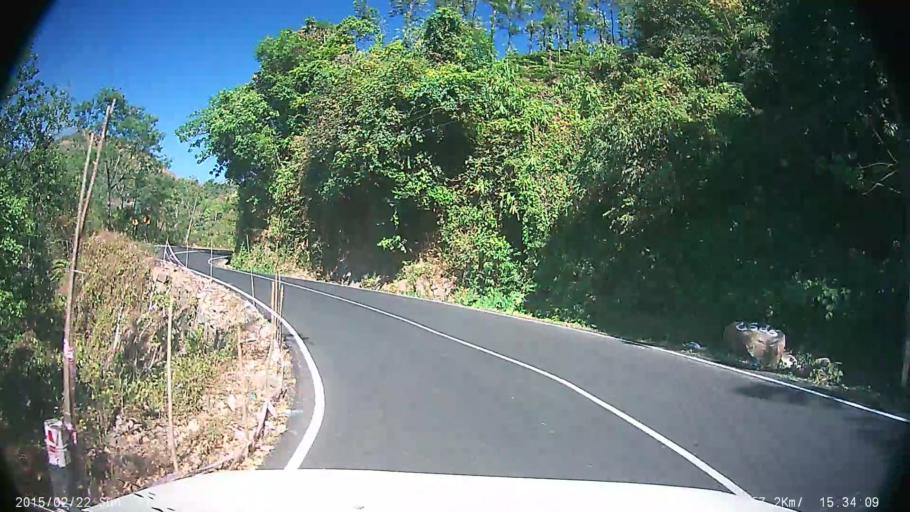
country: IN
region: Kerala
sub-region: Kottayam
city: Erattupetta
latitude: 9.5543
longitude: 76.9697
